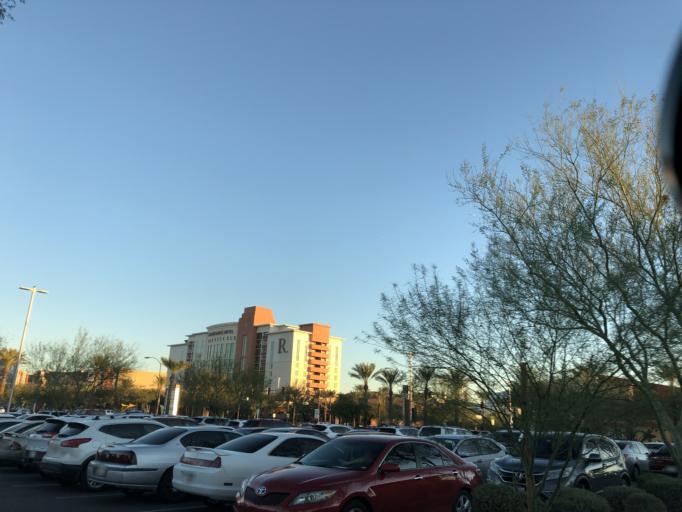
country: US
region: Arizona
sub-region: Maricopa County
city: Peoria
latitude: 33.5338
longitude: -112.2657
